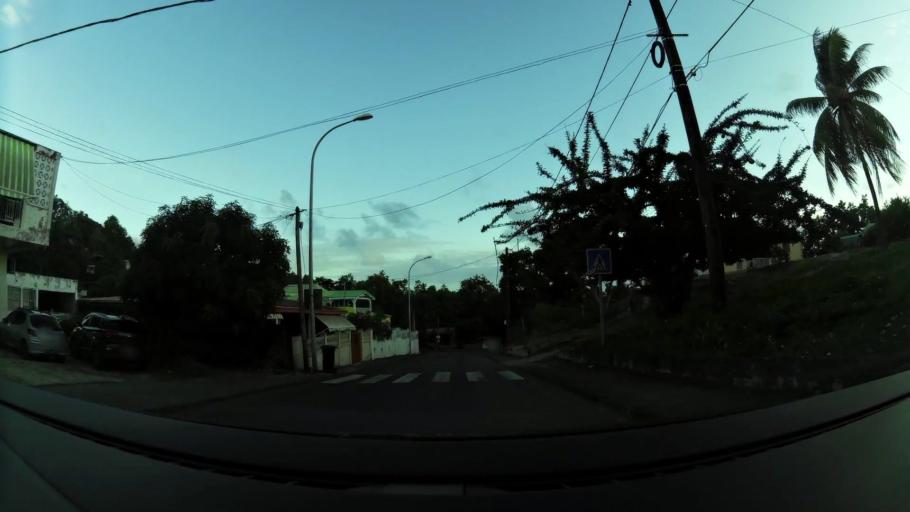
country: GP
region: Guadeloupe
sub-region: Guadeloupe
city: Les Abymes
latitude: 16.2646
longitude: -61.5005
